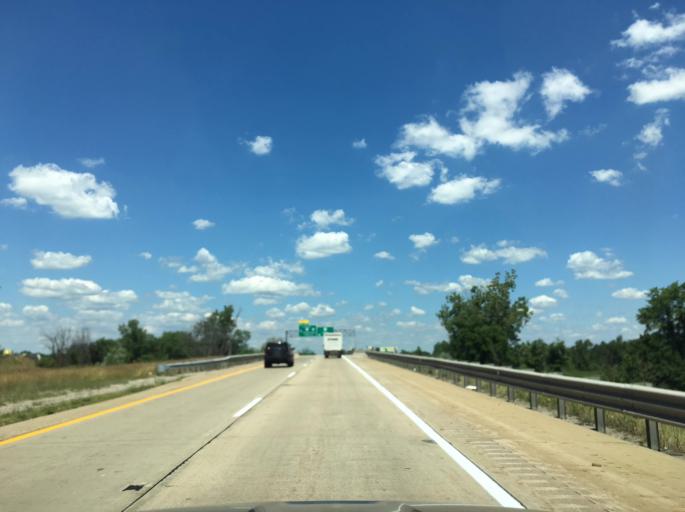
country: US
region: Michigan
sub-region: Midland County
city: Midland
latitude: 43.6075
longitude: -84.1628
